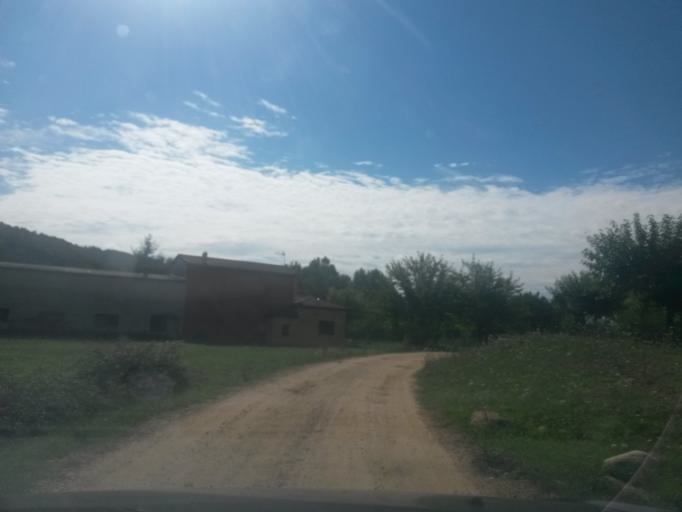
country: ES
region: Catalonia
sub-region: Provincia de Girona
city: la Cellera de Ter
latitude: 41.9853
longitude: 2.6222
